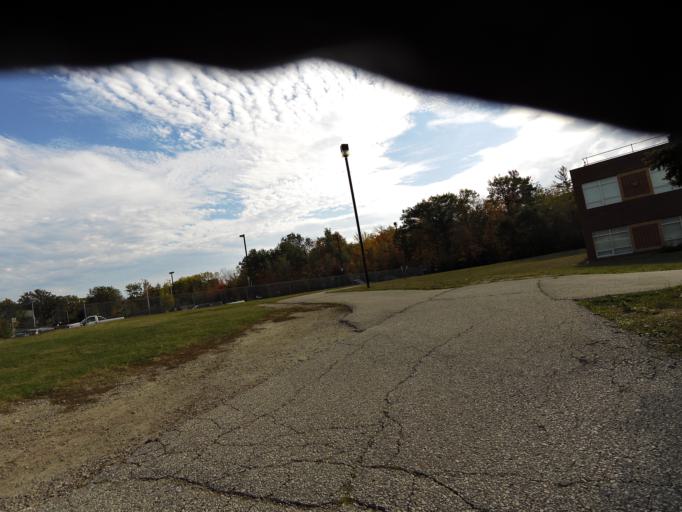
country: CA
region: Ontario
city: Mississauga
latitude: 43.5426
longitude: -79.6857
